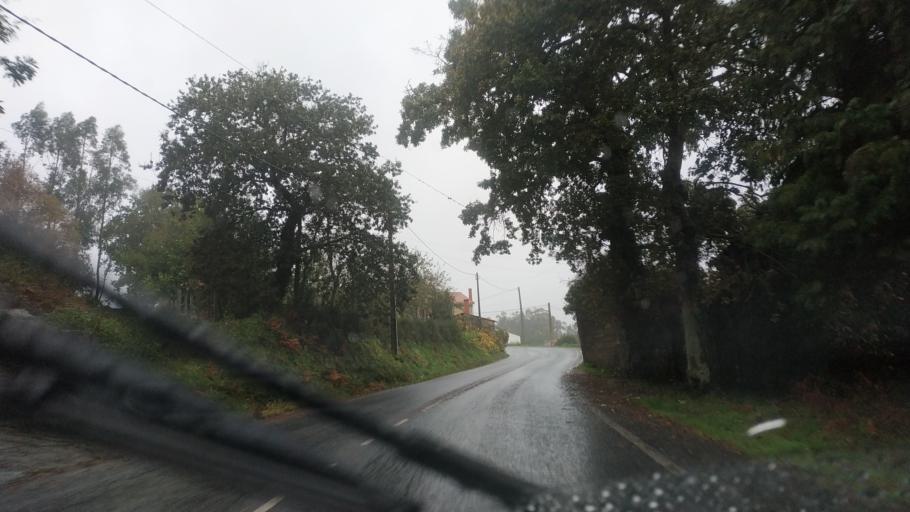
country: ES
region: Galicia
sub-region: Provincia da Coruna
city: Negreira
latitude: 42.9106
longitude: -8.7638
